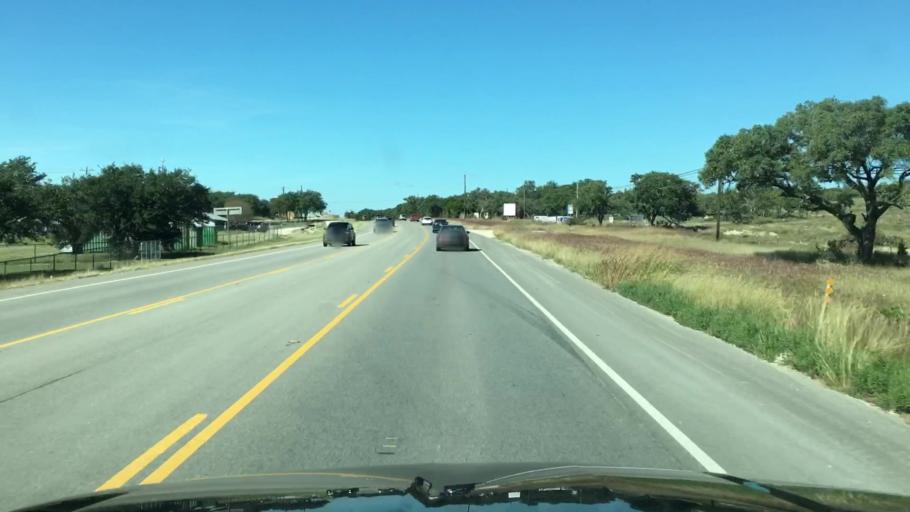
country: US
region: Texas
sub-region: Hays County
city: Dripping Springs
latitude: 30.1992
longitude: -98.1821
